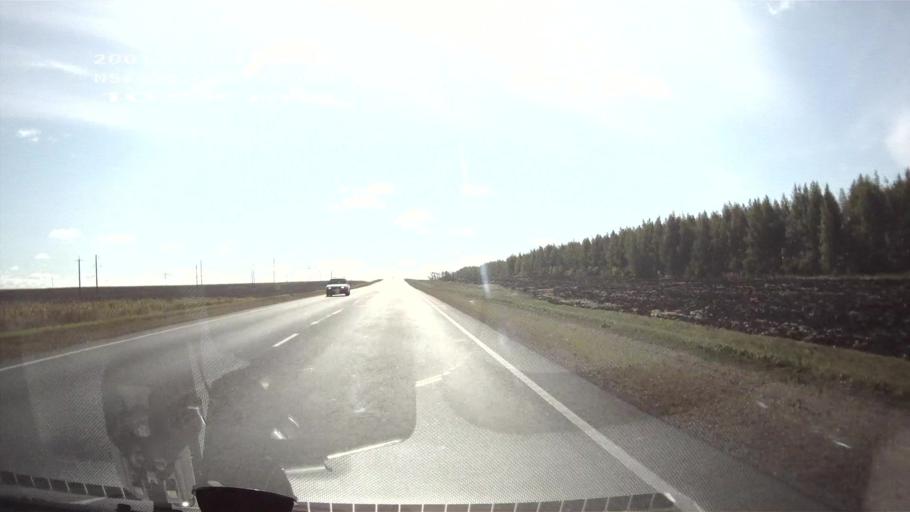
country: RU
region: Ulyanovsk
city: Tsil'na
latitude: 54.5857
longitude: 47.8839
